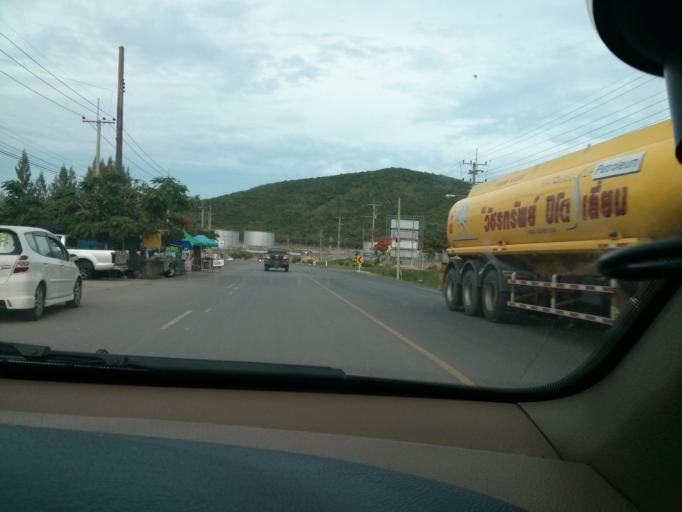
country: TH
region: Chon Buri
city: Sattahip
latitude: 12.6233
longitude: 100.9304
